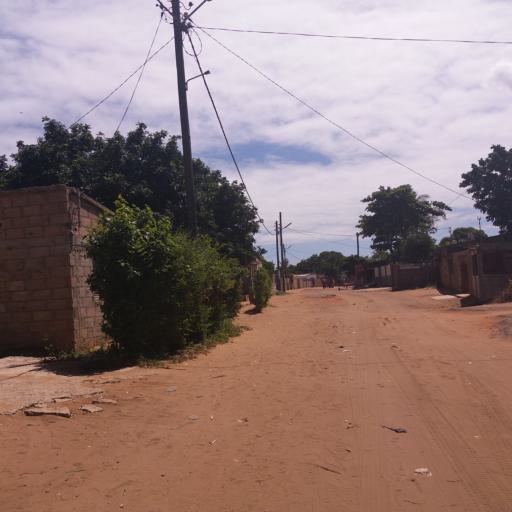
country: MZ
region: Maputo City
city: Maputo
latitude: -25.9077
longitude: 32.5902
